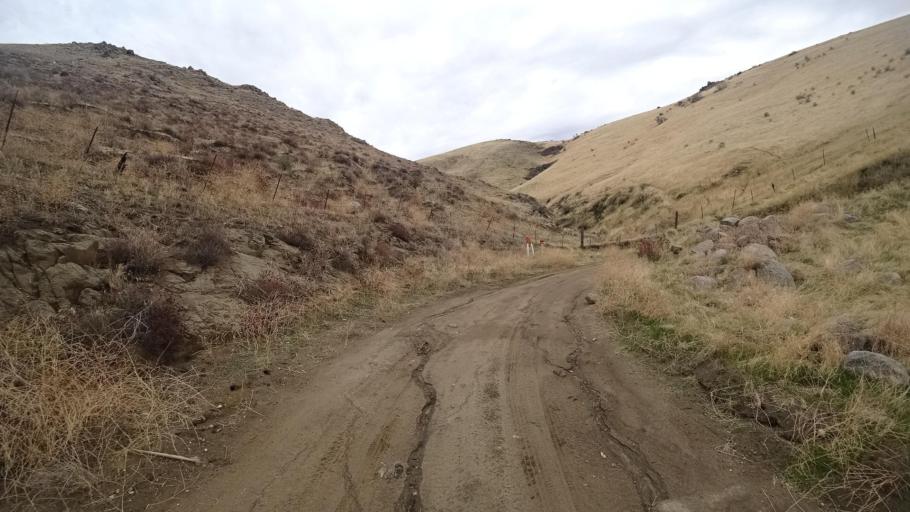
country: US
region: California
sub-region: Kern County
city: Arvin
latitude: 35.1324
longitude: -118.7664
